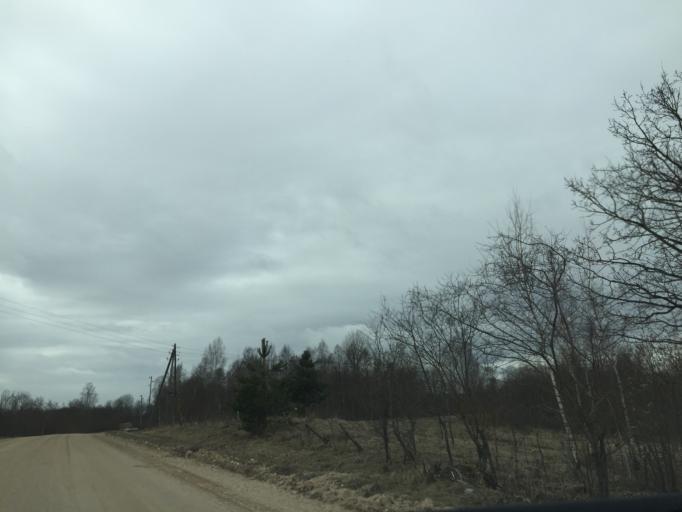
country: LV
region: Kraslavas Rajons
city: Kraslava
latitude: 55.9797
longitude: 27.1006
